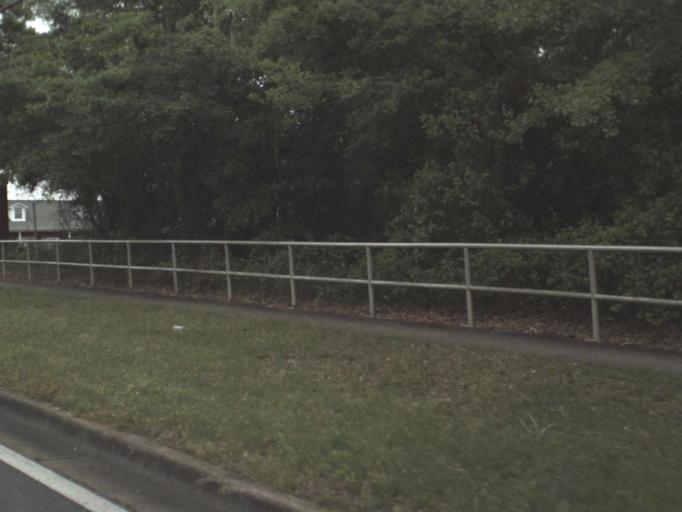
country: US
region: Florida
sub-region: Escambia County
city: Brent
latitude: 30.4614
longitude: -87.2696
